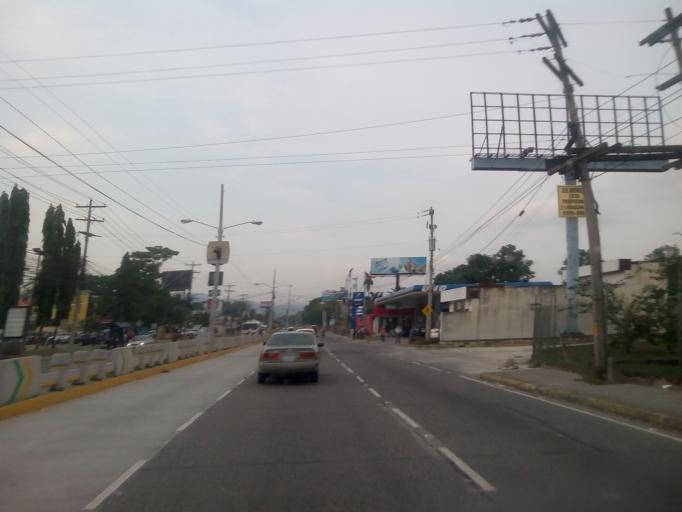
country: HN
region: Cortes
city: San Pedro Sula
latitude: 15.5327
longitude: -88.0193
